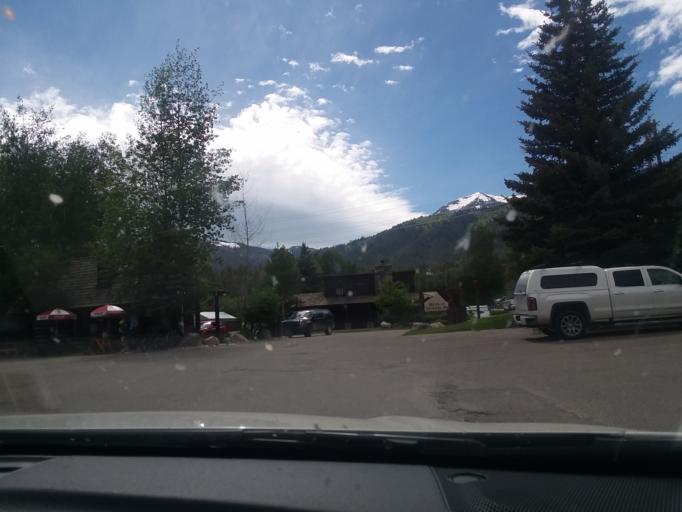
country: US
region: Wyoming
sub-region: Teton County
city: Wilson
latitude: 43.4978
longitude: -110.8735
